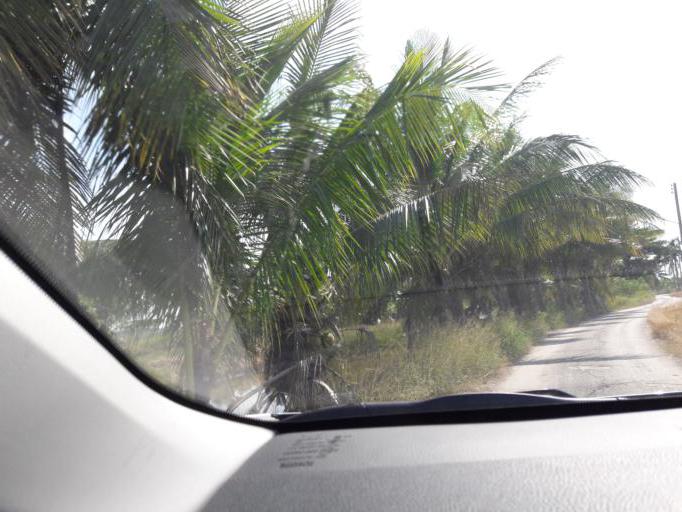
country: TH
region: Ang Thong
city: Wiset Chaichan
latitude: 14.5605
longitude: 100.3937
